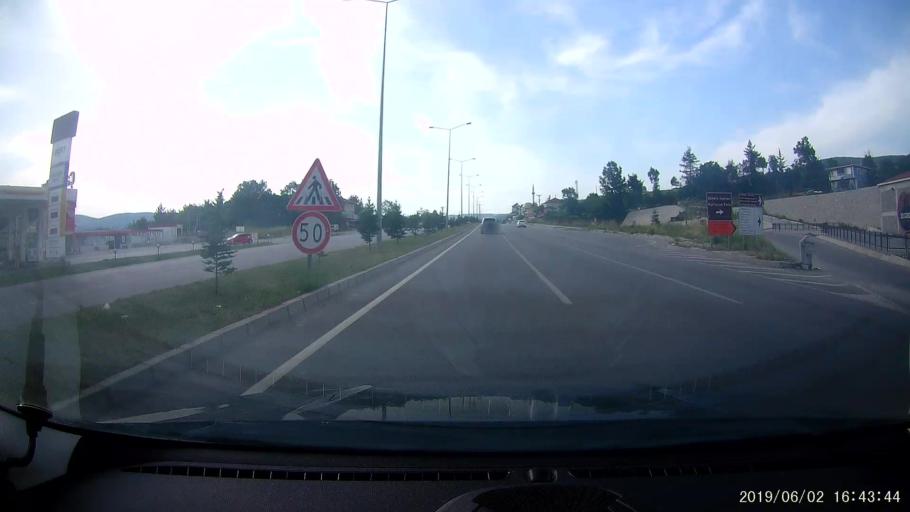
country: TR
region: Samsun
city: Kavak
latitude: 41.1400
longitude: 36.1218
